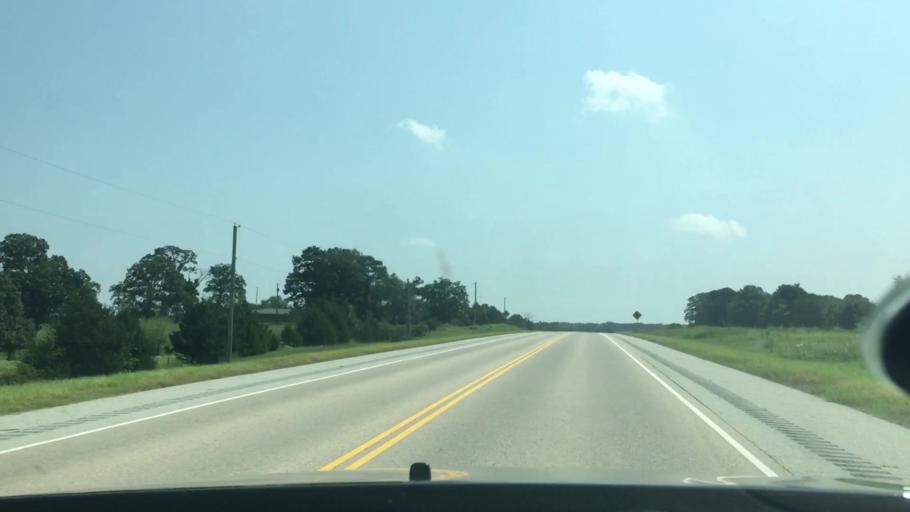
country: US
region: Oklahoma
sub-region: Atoka County
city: Atoka
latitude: 34.2892
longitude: -95.9679
